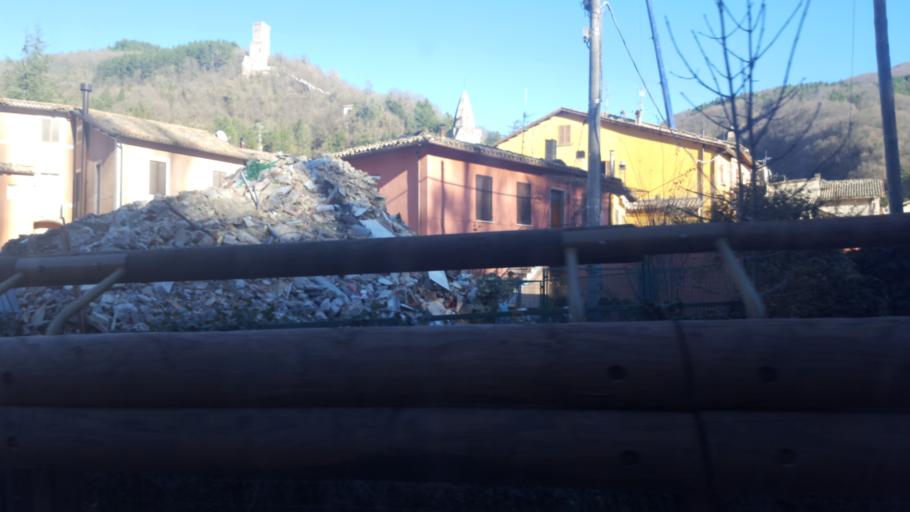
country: IT
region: The Marches
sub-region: Provincia di Macerata
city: Visso
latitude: 42.9309
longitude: 13.0858
